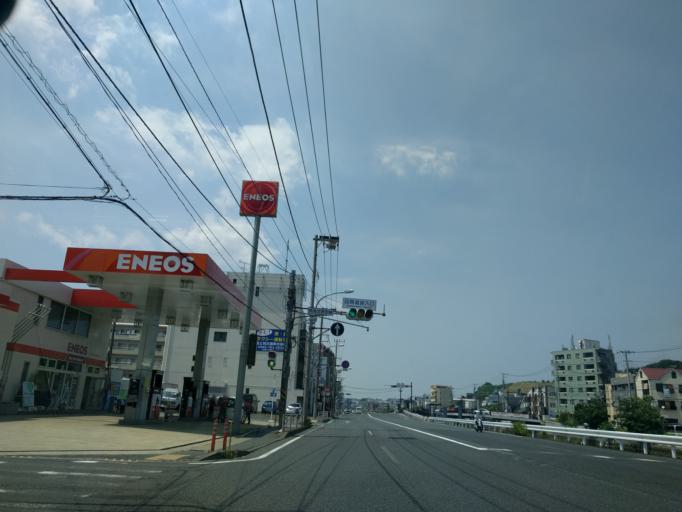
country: JP
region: Kanagawa
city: Yokohama
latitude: 35.4212
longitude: 139.6250
